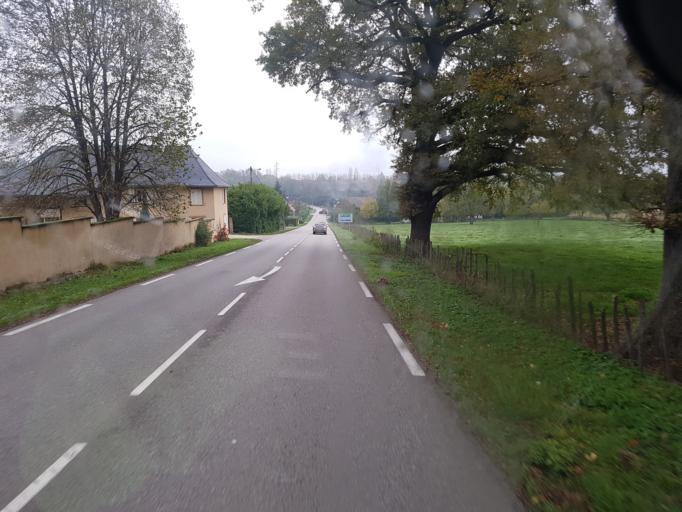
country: FR
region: Rhone-Alpes
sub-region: Departement de l'Isere
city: Les Abrets
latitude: 45.5540
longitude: 5.5915
